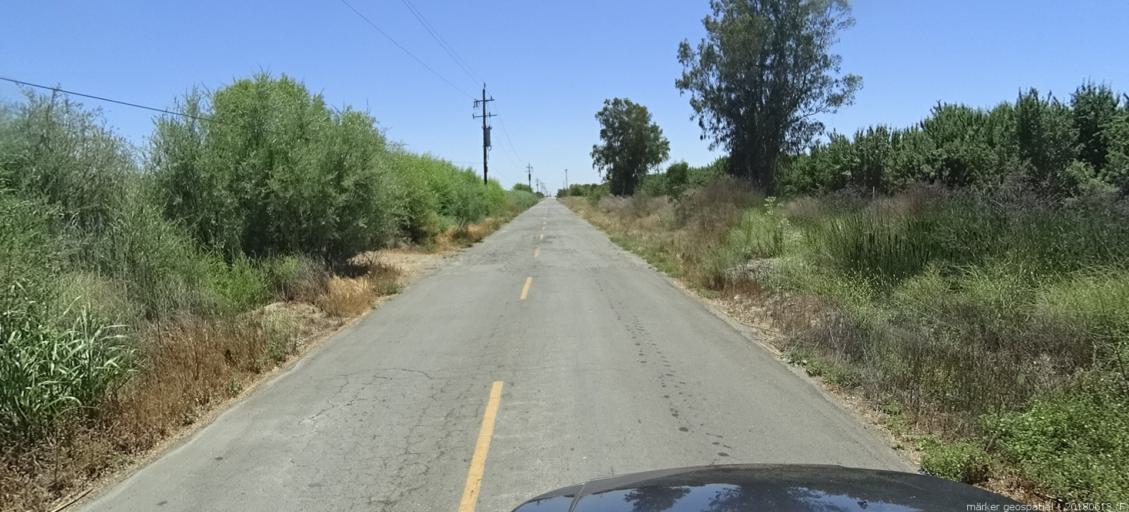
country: US
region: California
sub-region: Madera County
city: Fairmead
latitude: 36.9996
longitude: -120.2742
